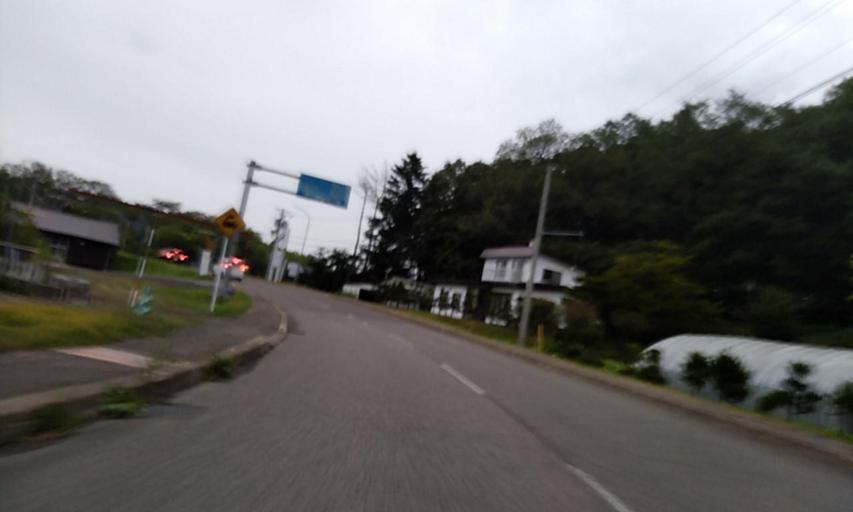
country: JP
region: Hokkaido
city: Abashiri
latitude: 44.0035
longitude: 144.2312
